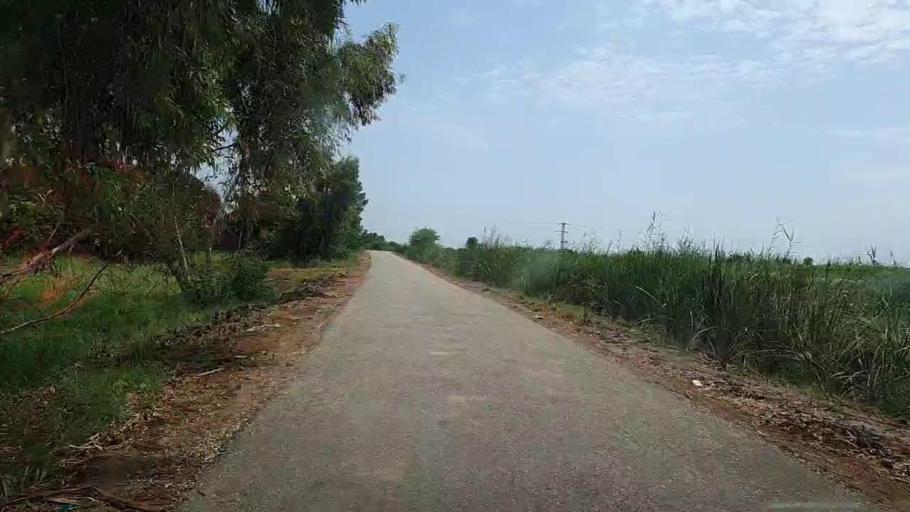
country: PK
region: Sindh
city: Bhiria
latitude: 26.9037
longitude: 68.2002
